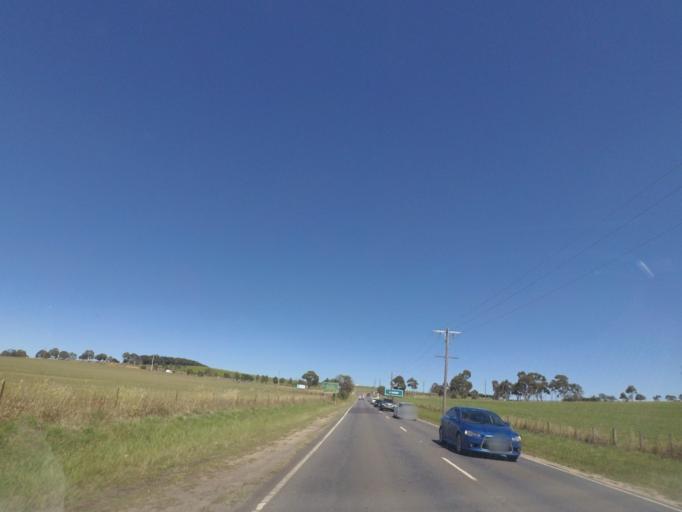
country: AU
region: Victoria
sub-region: Hume
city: Craigieburn
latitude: -37.5337
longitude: 144.8883
